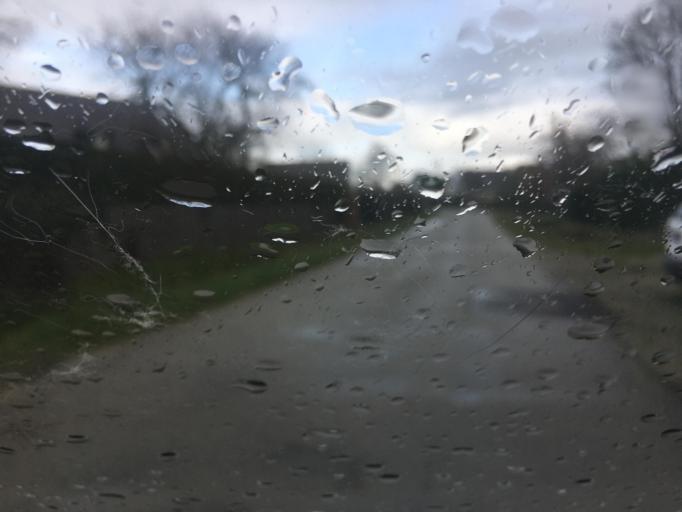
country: FR
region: Brittany
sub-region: Departement du Morbihan
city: Surzur
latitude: 47.5155
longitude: -2.6693
